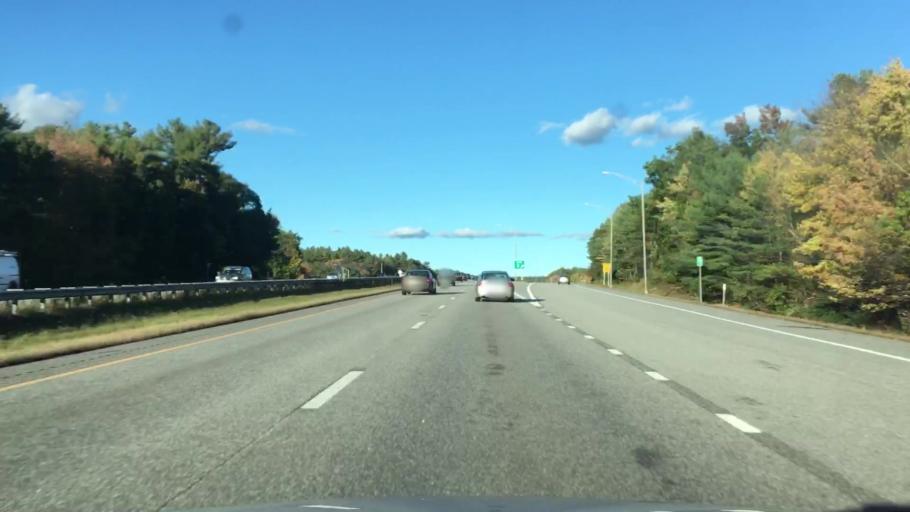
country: US
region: New Hampshire
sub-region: Rockingham County
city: Auburn
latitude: 43.0205
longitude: -71.3700
